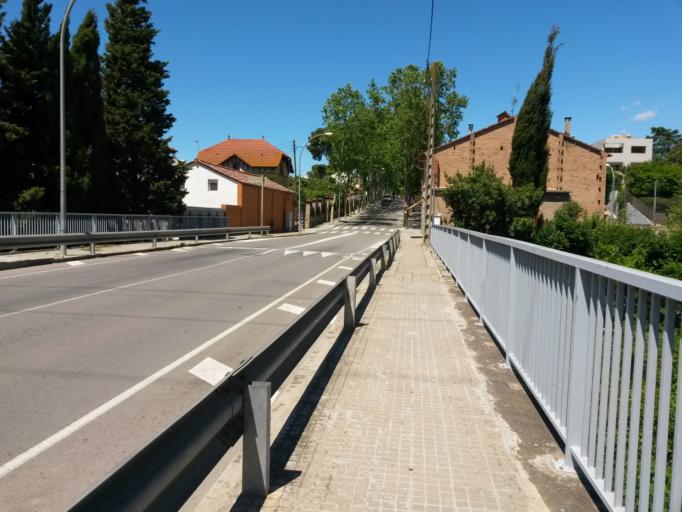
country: ES
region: Catalonia
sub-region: Provincia de Barcelona
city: Cerdanyola del Valles
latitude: 41.4826
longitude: 2.1328
